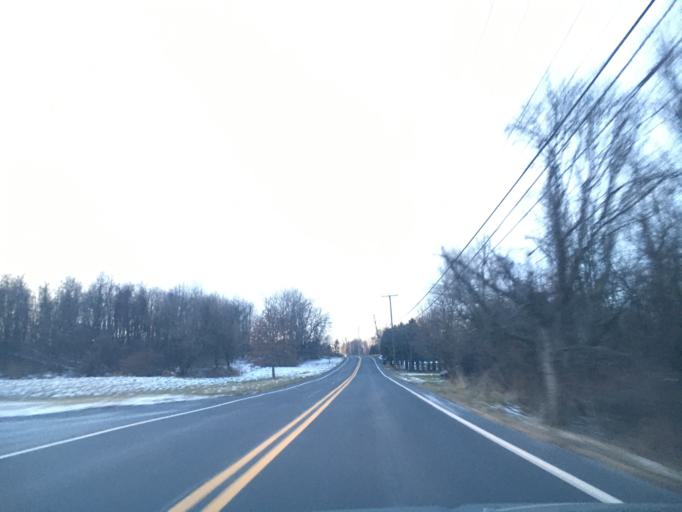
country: US
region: Pennsylvania
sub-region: Northampton County
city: Bath
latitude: 40.7814
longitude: -75.4034
